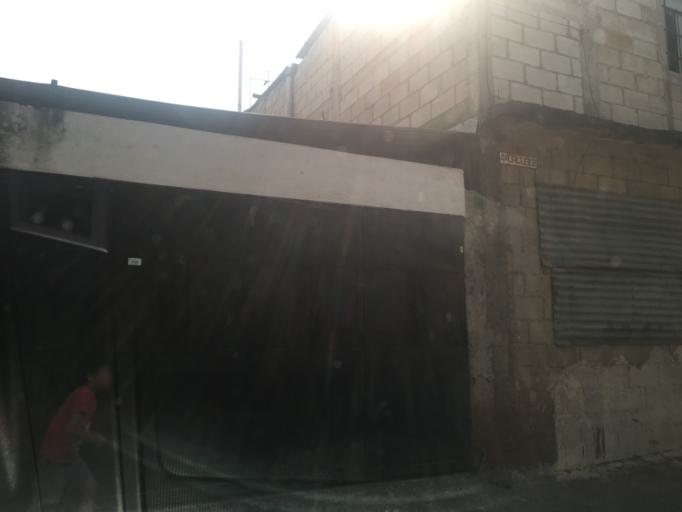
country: GT
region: Guatemala
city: Santa Catarina Pinula
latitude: 14.5432
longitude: -90.5108
